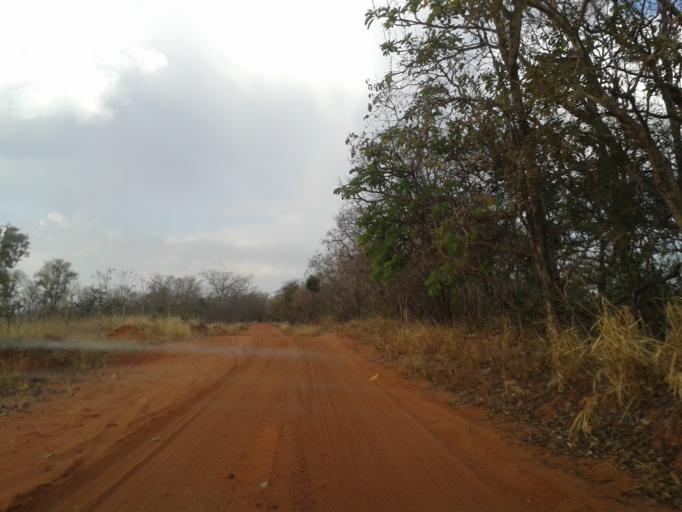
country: BR
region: Minas Gerais
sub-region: Santa Vitoria
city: Santa Vitoria
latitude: -19.1861
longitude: -49.8634
